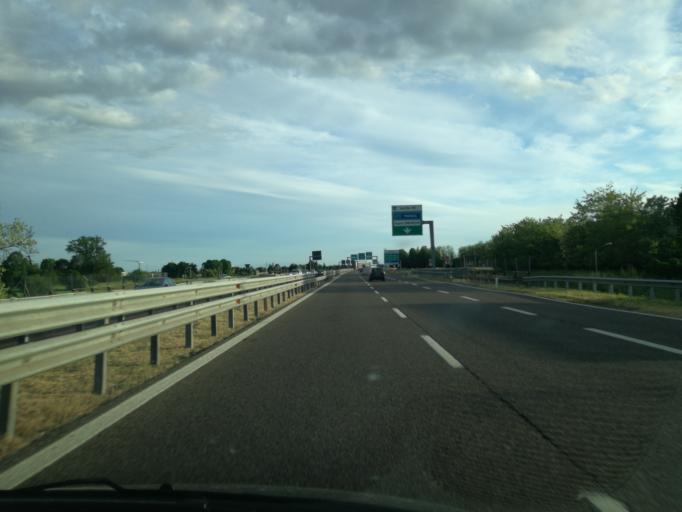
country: IT
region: Lombardy
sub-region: Provincia di Monza e Brianza
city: Agrate Brianza
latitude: 45.5780
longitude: 9.3424
